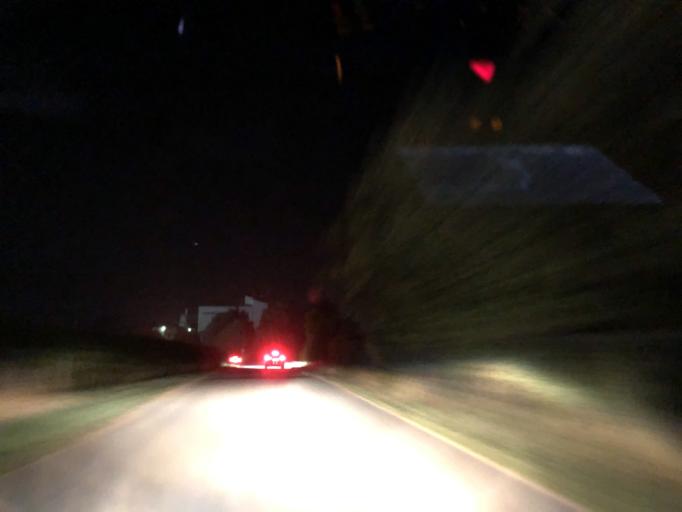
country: DE
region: North Rhine-Westphalia
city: Warstein
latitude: 51.4304
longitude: 8.3617
